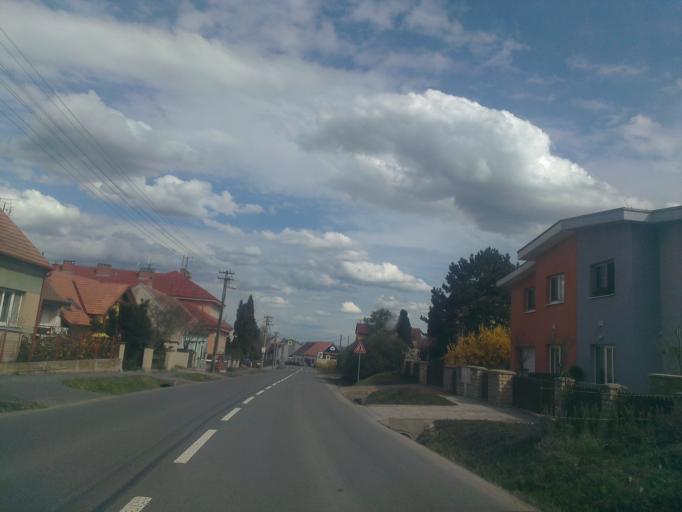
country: CZ
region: South Moravian
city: Zelesice
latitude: 49.1154
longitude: 16.5723
